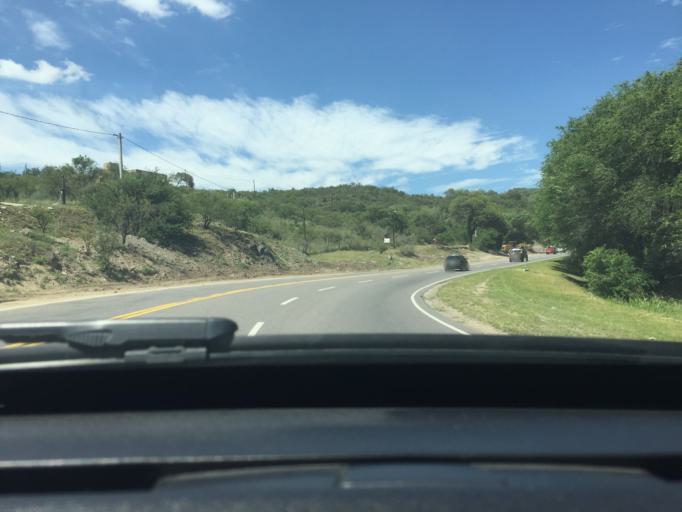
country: AR
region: Cordoba
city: Alta Gracia
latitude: -31.7395
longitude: -64.4533
